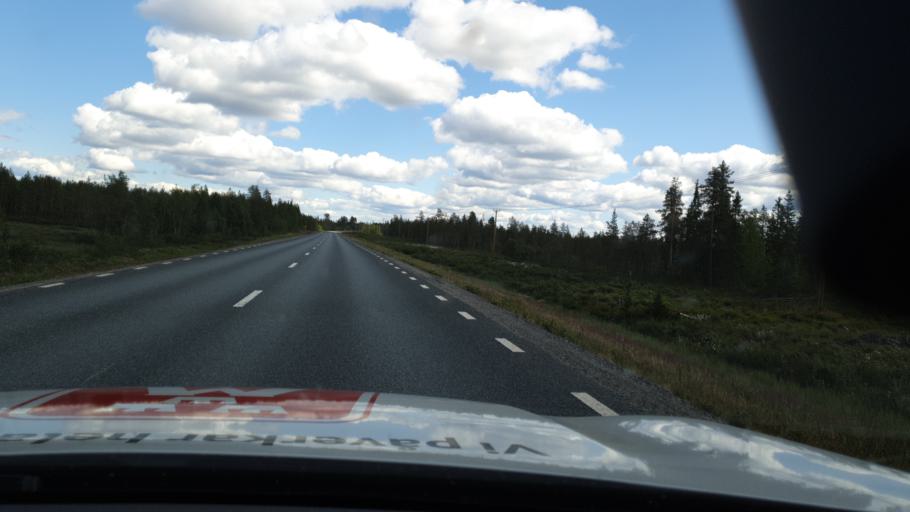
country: SE
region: Vaesterbotten
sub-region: Sorsele Kommun
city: Sorsele
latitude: 65.5595
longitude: 17.8043
